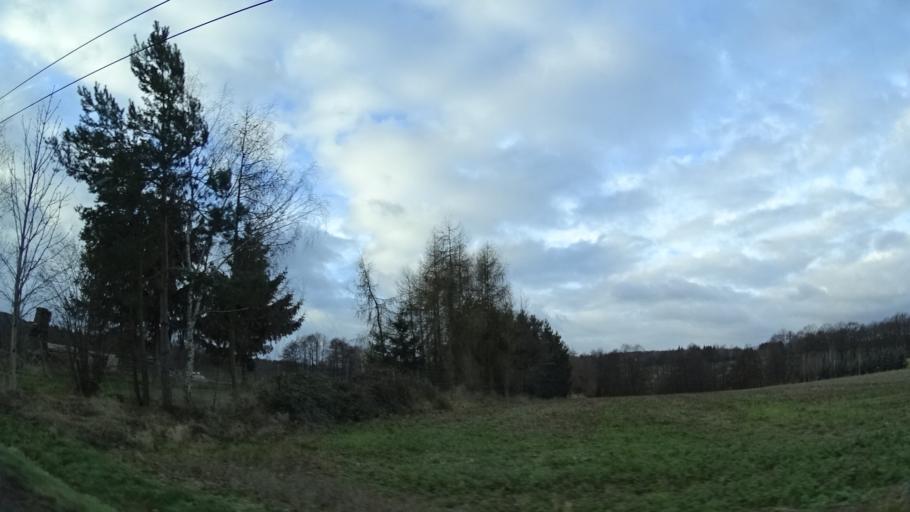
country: DE
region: Thuringia
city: Zeulenroda
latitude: 50.6358
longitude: 11.9888
